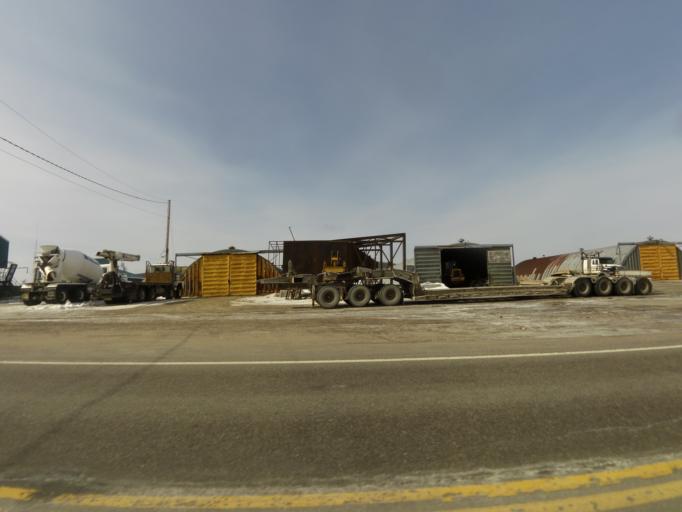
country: CA
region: Quebec
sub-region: Laurentides
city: Mont-Laurier
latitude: 46.5839
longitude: -75.4751
